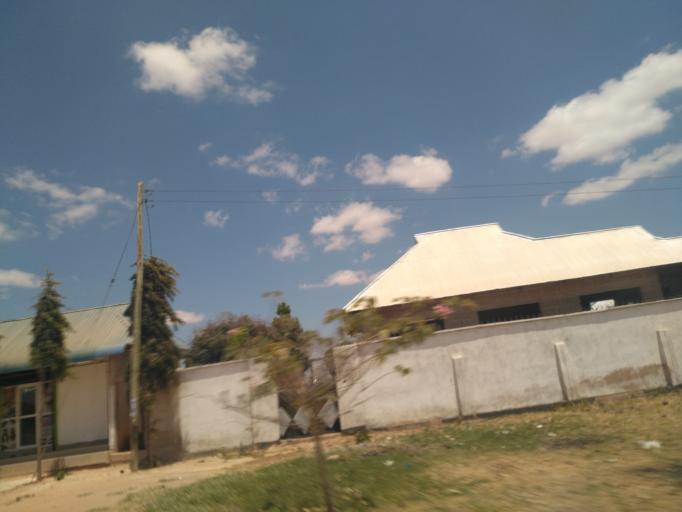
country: TZ
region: Dodoma
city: Kisasa
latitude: -6.1704
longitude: 35.7912
